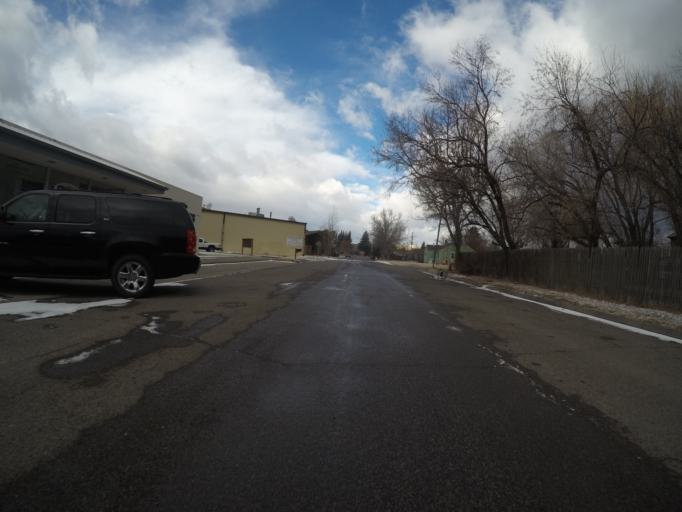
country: US
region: Montana
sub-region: Park County
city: Livingston
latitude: 45.6524
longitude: -110.5701
